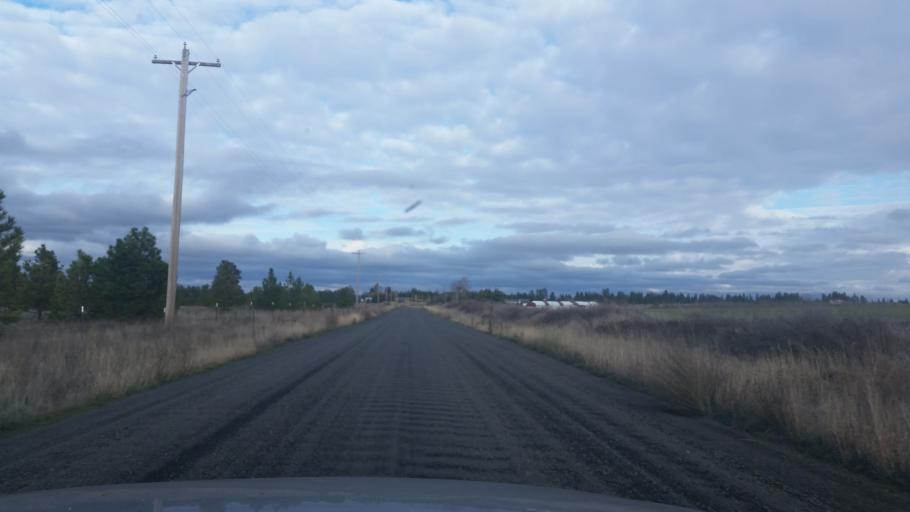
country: US
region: Washington
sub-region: Spokane County
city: Cheney
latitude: 47.4172
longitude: -117.4768
